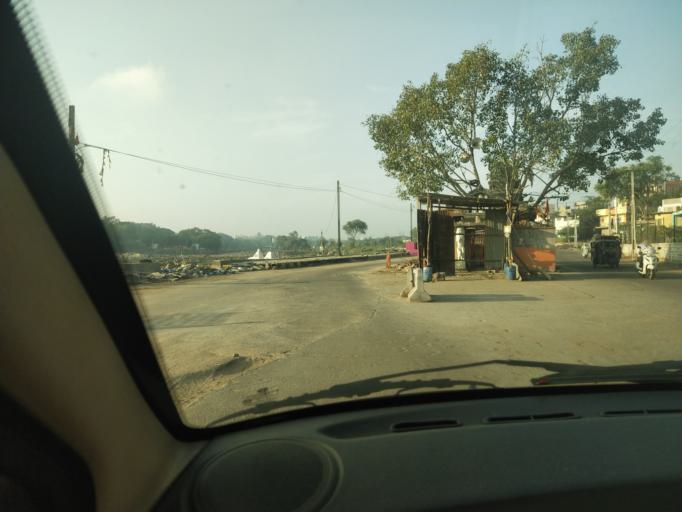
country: IN
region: Telangana
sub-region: Hyderabad
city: Hyderabad
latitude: 17.3676
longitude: 78.4570
